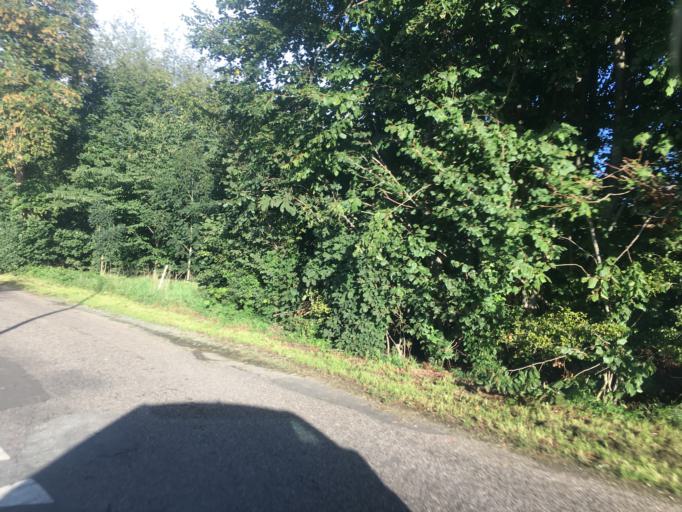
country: DE
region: Schleswig-Holstein
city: Ellhoft
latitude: 54.9619
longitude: 9.0123
